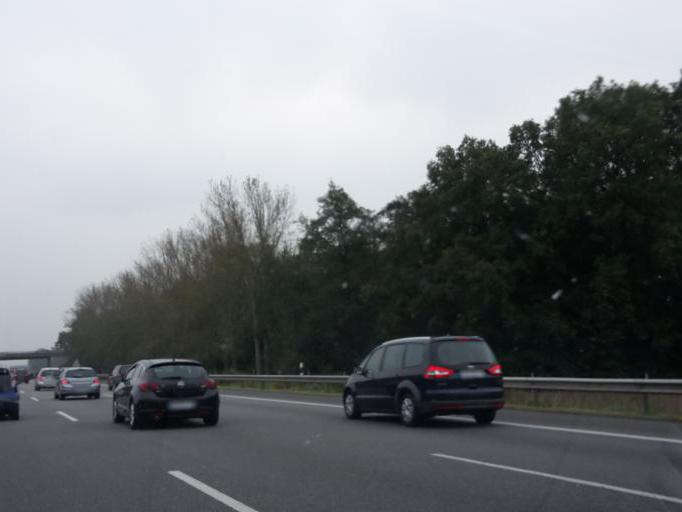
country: DE
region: Lower Saxony
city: Bakum
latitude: 52.6973
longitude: 8.1733
